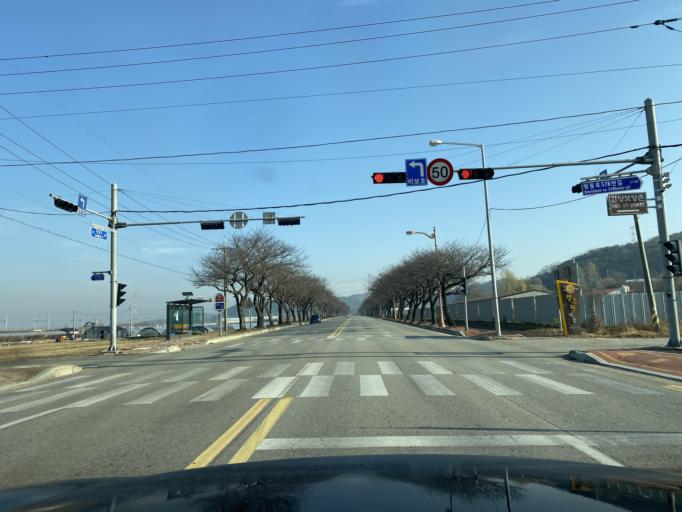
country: KR
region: Chungcheongnam-do
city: Yesan
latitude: 36.7280
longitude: 126.8551
